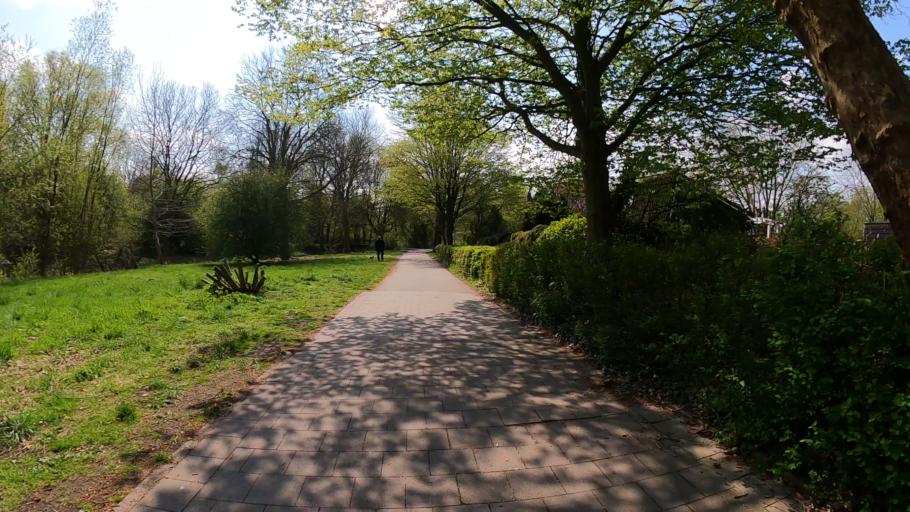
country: DE
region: Hamburg
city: Steilshoop
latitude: 53.6111
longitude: 10.0665
